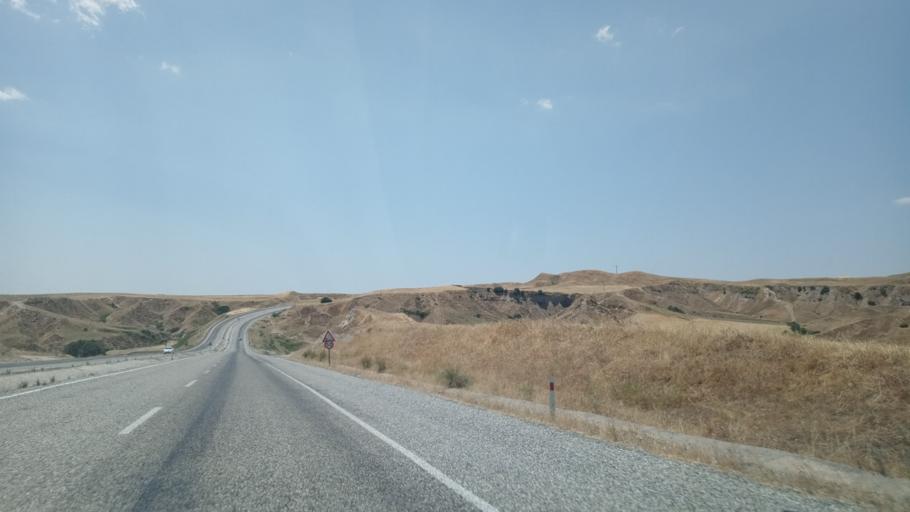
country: TR
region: Batman
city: Bekirhan
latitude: 38.1414
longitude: 41.2779
